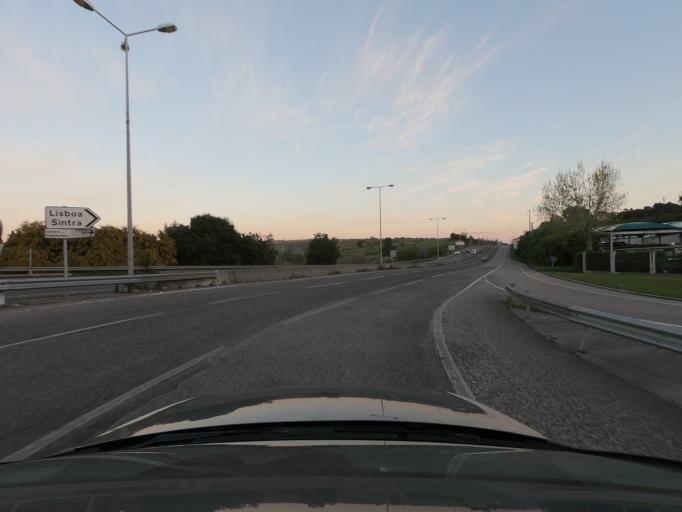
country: PT
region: Lisbon
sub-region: Sintra
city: Queluz
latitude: 38.7531
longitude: -9.2646
